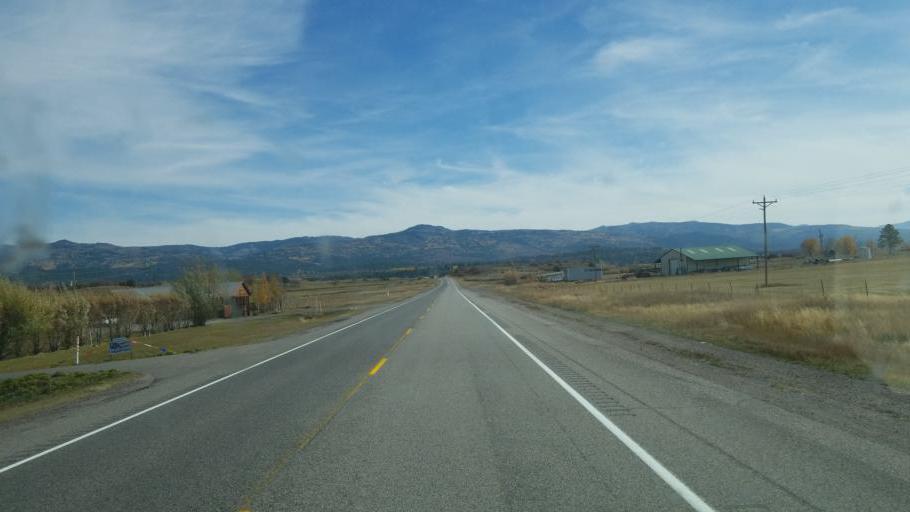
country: US
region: New Mexico
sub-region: Rio Arriba County
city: Chama
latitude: 36.8851
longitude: -106.6089
